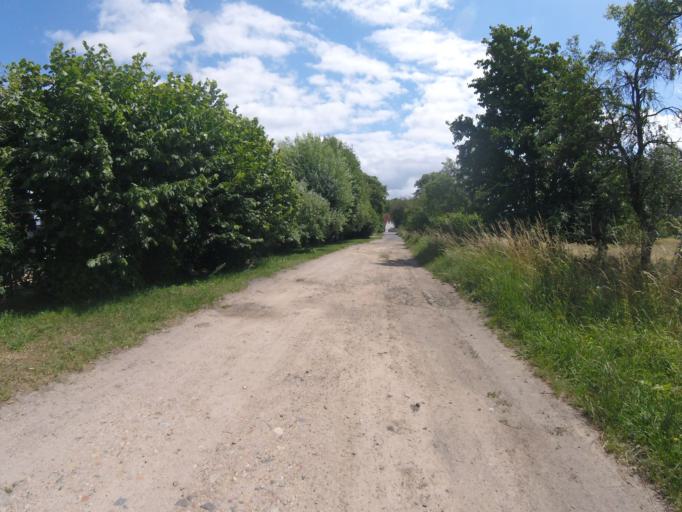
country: DE
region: Brandenburg
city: Mittenwalde
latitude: 52.2436
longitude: 13.5567
